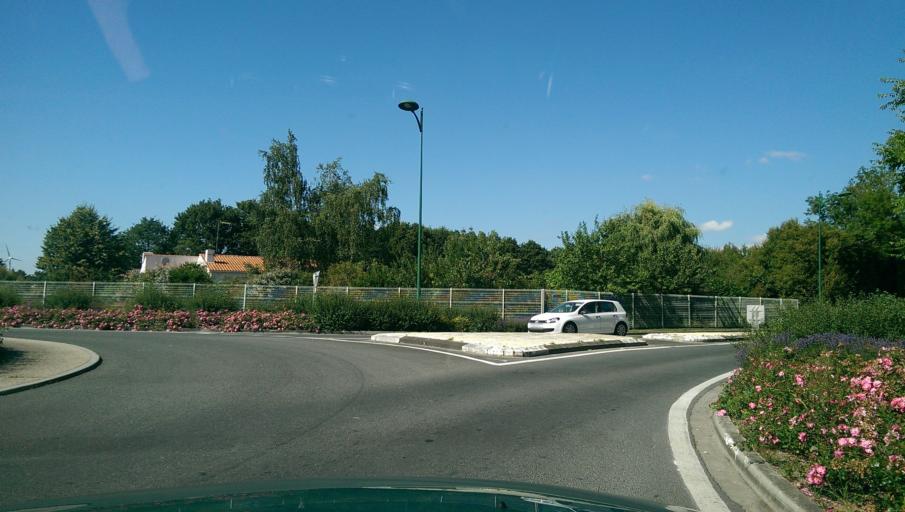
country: FR
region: Pays de la Loire
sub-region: Departement de la Vendee
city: Falleron
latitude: 46.8800
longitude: -1.7097
